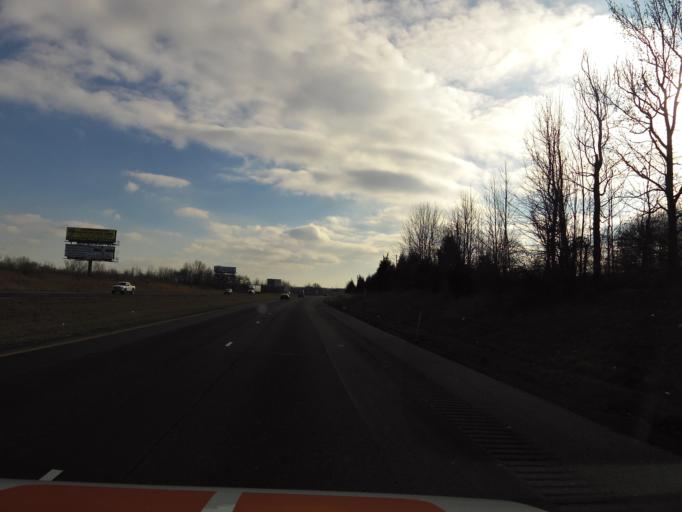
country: US
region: Indiana
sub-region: Scott County
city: Scottsburg
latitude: 38.6704
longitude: -85.7835
